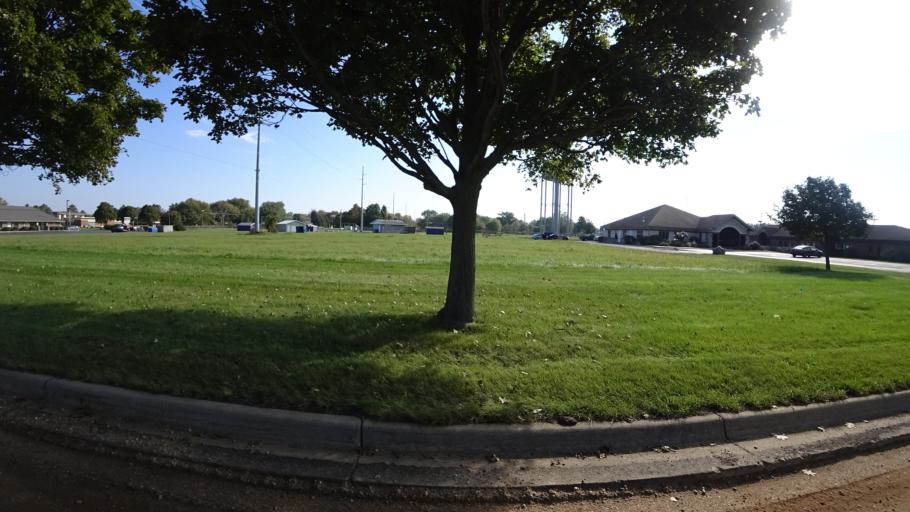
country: US
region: Michigan
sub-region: Saint Joseph County
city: Three Rivers
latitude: 41.9336
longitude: -85.6469
